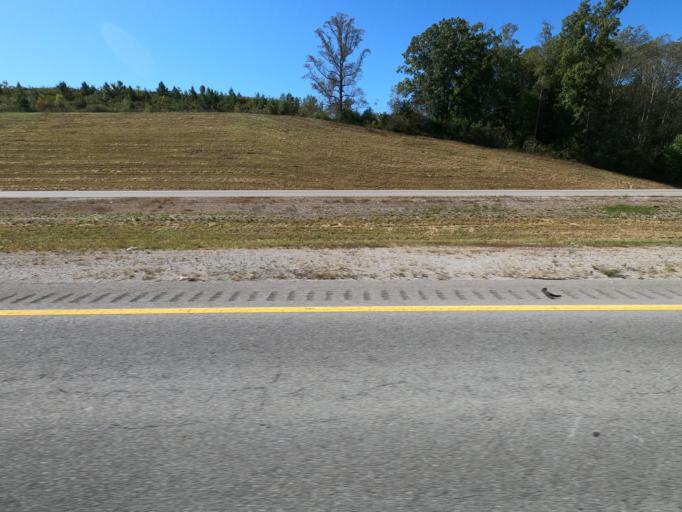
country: US
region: Tennessee
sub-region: Williamson County
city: Fairview
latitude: 35.8586
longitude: -87.0802
